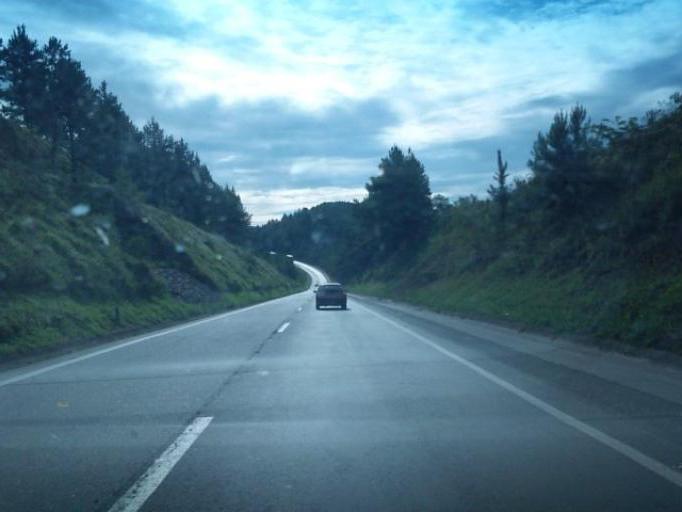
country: BR
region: Parana
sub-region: Campina Grande Do Sul
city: Campina Grande do Sul
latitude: -25.1053
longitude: -48.8427
